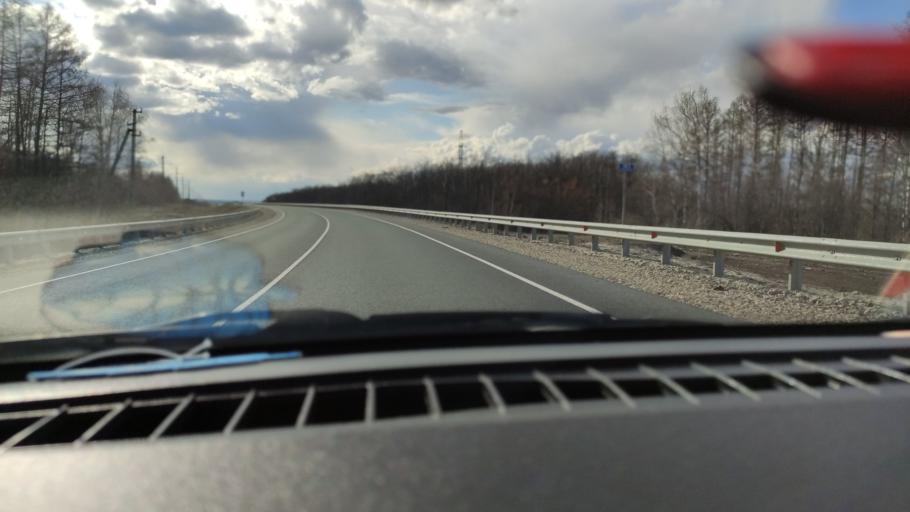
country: RU
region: Saratov
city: Shikhany
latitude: 52.1613
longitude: 47.1575
